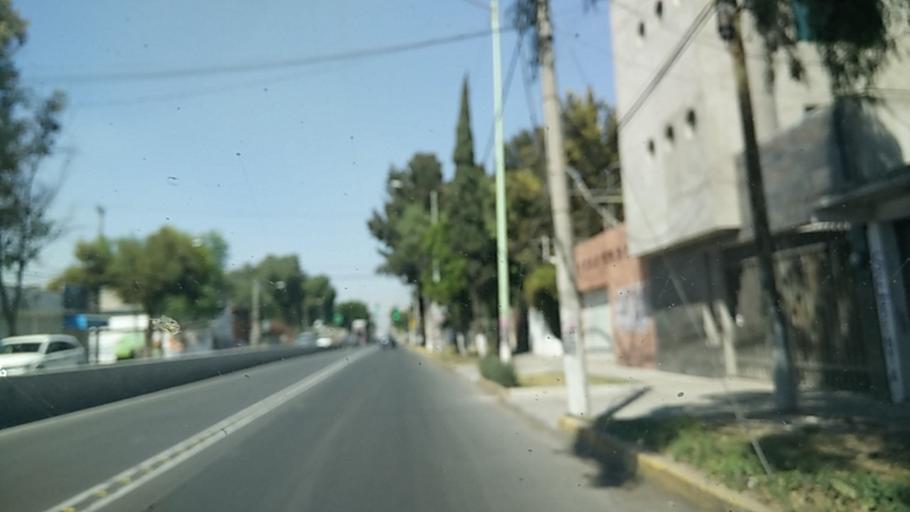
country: MX
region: Mexico
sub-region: Atenco
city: Colonia el Salado
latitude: 19.5921
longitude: -99.0284
